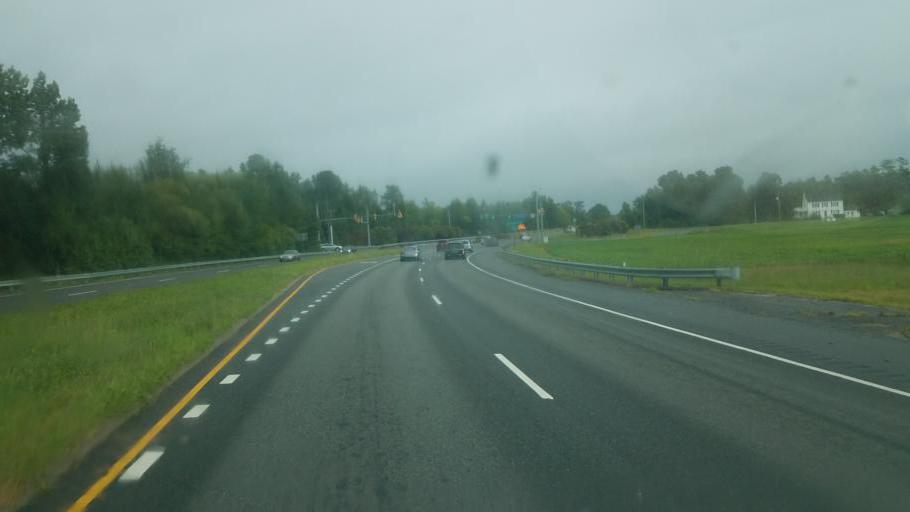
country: US
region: North Carolina
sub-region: Currituck County
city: Moyock
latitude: 36.5625
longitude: -76.1986
